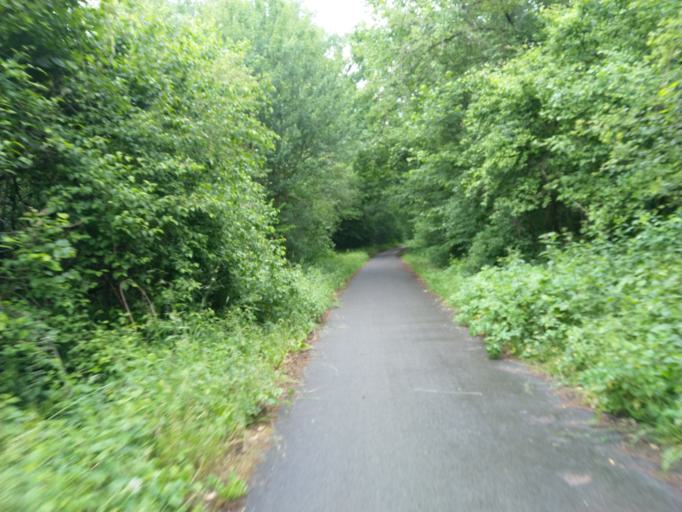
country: BE
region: Wallonia
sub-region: Province de Namur
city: Anhee
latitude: 50.3166
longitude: 4.8377
